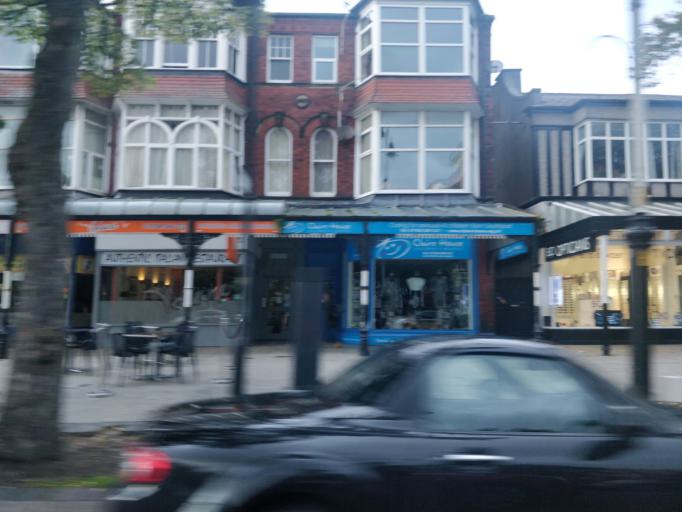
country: GB
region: England
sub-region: Sefton
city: Southport
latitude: 53.6515
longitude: -2.9999
